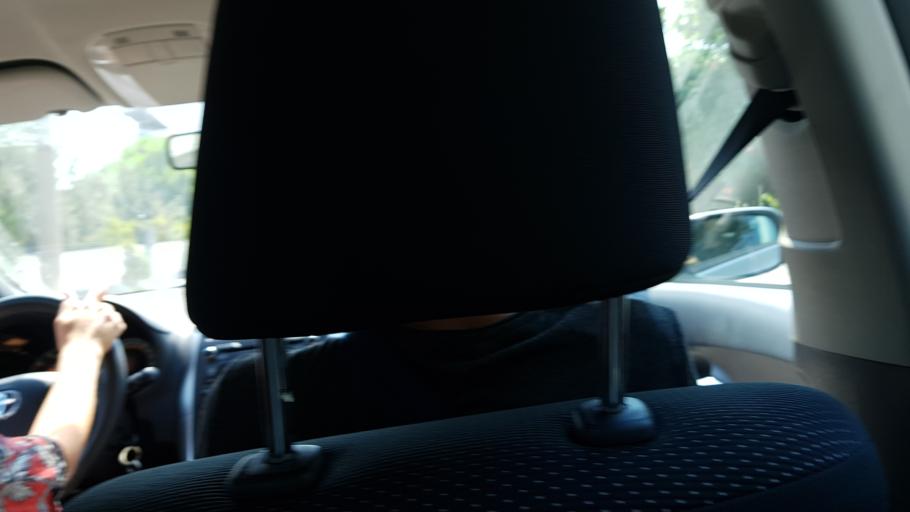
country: TR
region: Izmir
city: Urla
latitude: 38.3916
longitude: 26.7431
